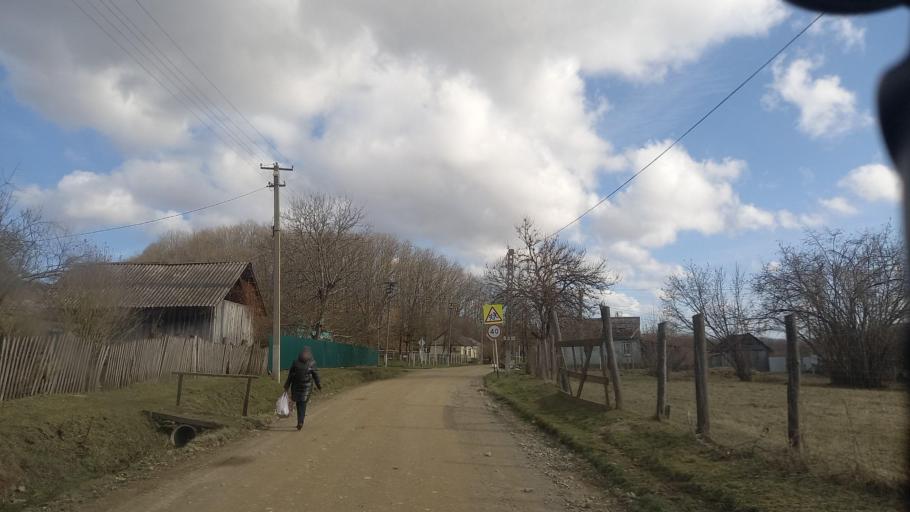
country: RU
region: Krasnodarskiy
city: Smolenskaya
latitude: 44.6043
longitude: 38.8551
